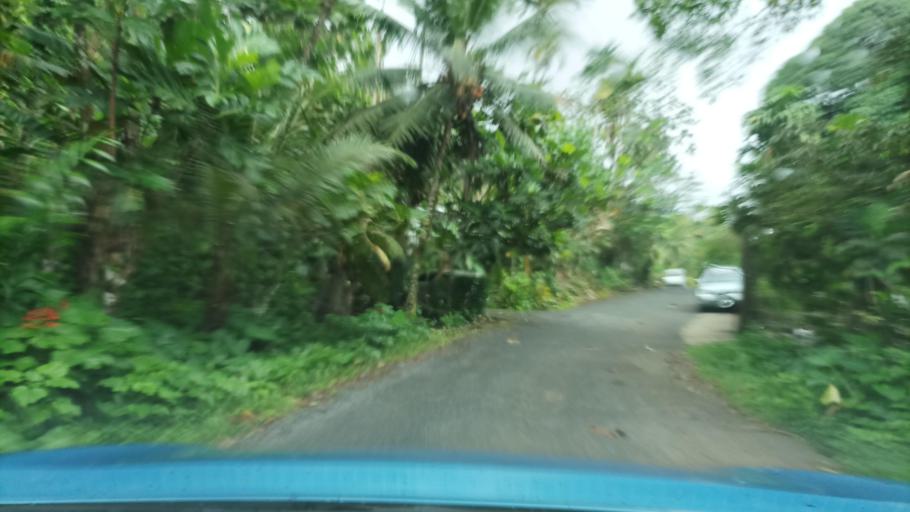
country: FM
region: Pohnpei
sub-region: Kolonia Municipality
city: Kolonia
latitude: 6.9579
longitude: 158.2256
